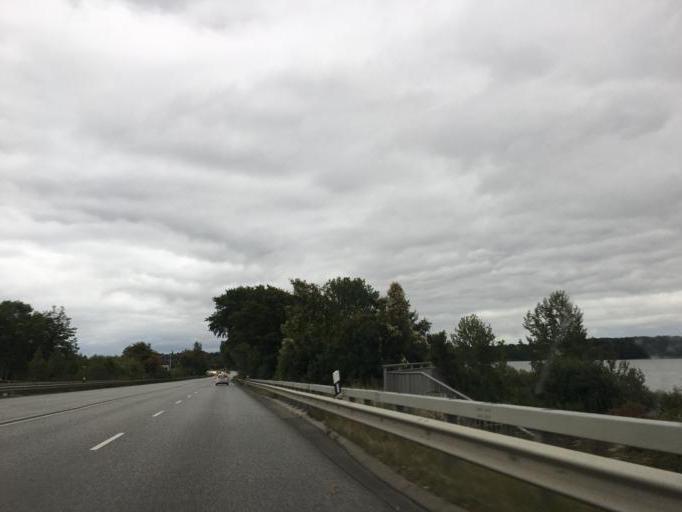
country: DE
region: Schleswig-Holstein
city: Windeby
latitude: 54.4761
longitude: 9.8229
